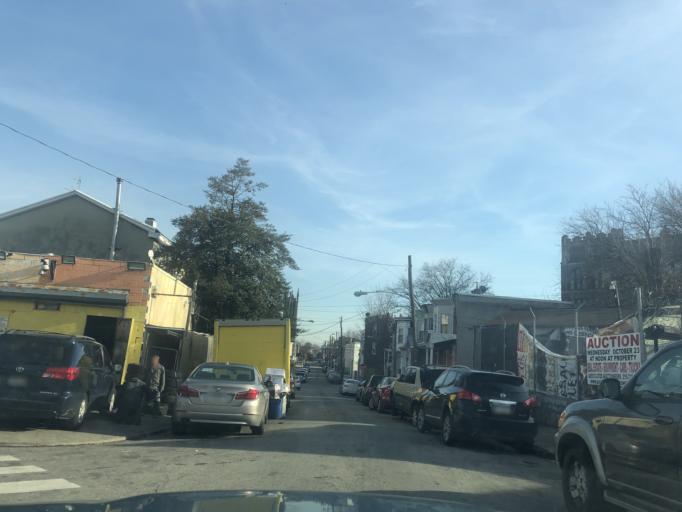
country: US
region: Pennsylvania
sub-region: Delaware County
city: Millbourne
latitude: 39.9771
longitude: -75.2288
